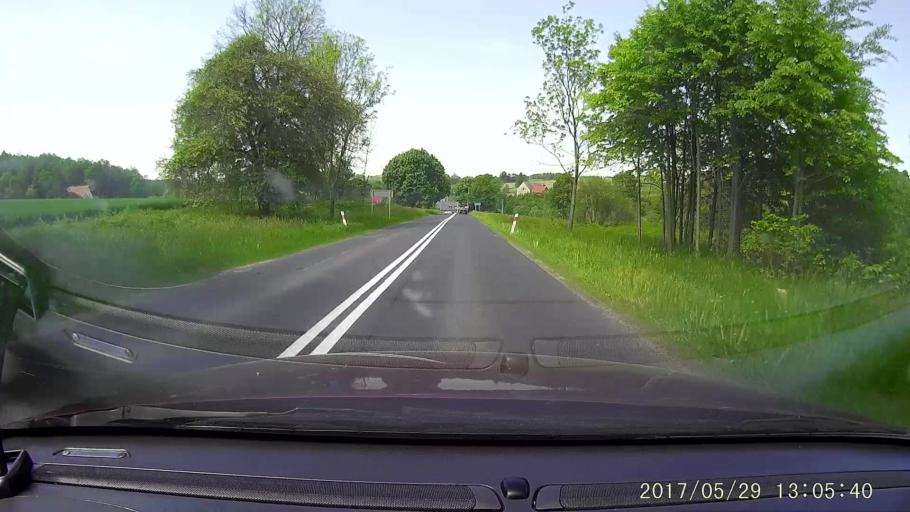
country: PL
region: Lower Silesian Voivodeship
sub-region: Powiat jeleniogorski
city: Stara Kamienica
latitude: 50.9462
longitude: 15.5879
